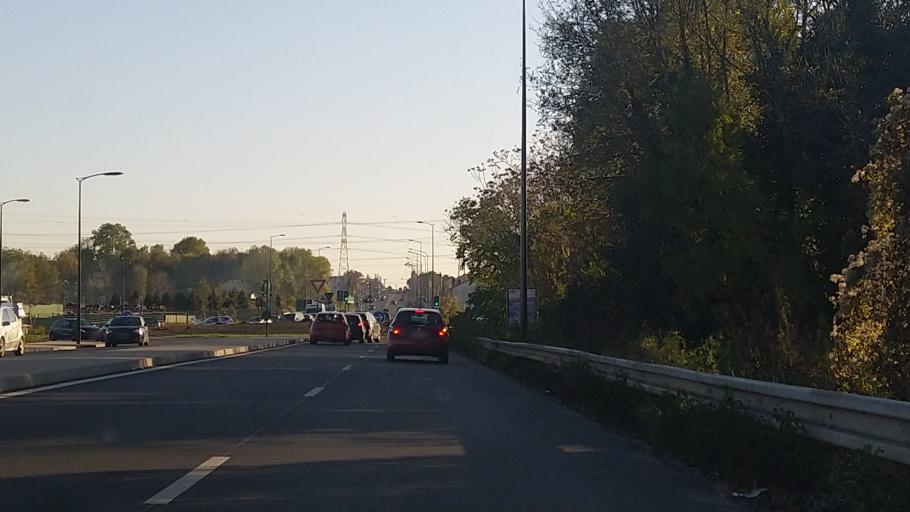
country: FR
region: Ile-de-France
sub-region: Departement du Val-d'Oise
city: Groslay
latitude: 48.9858
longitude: 2.3613
